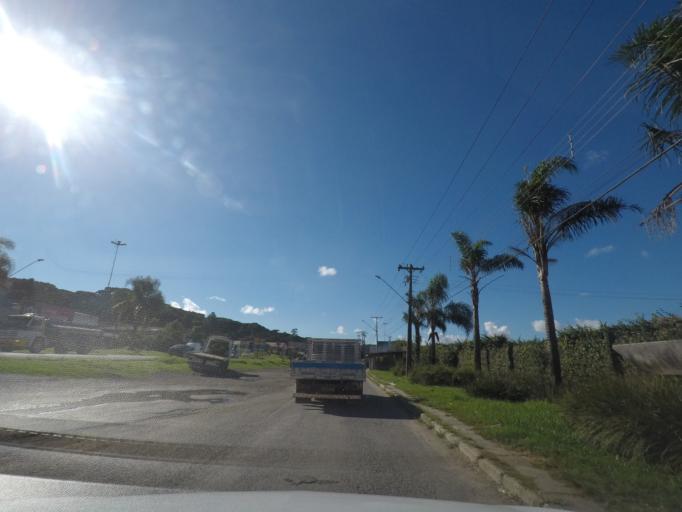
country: BR
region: Parana
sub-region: Almirante Tamandare
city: Almirante Tamandare
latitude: -25.3447
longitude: -49.2830
